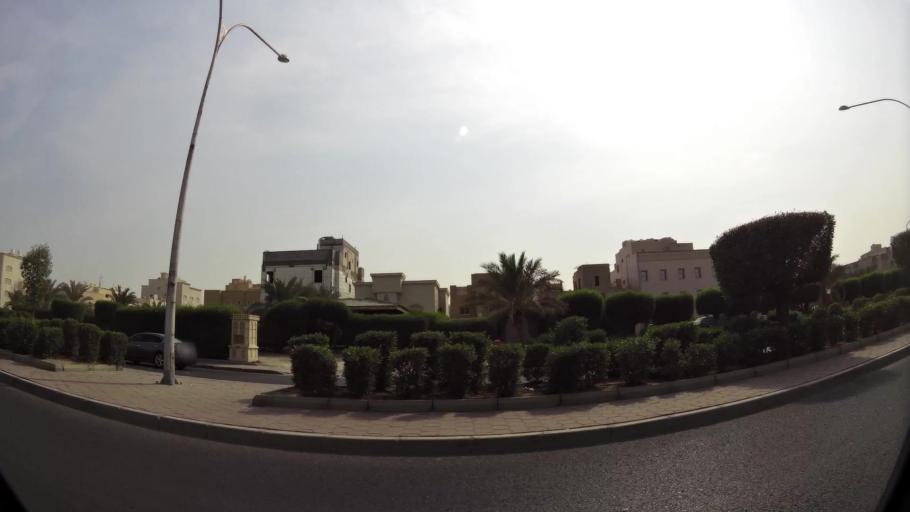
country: KW
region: Al Asimah
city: Ar Rabiyah
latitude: 29.2886
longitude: 47.9316
